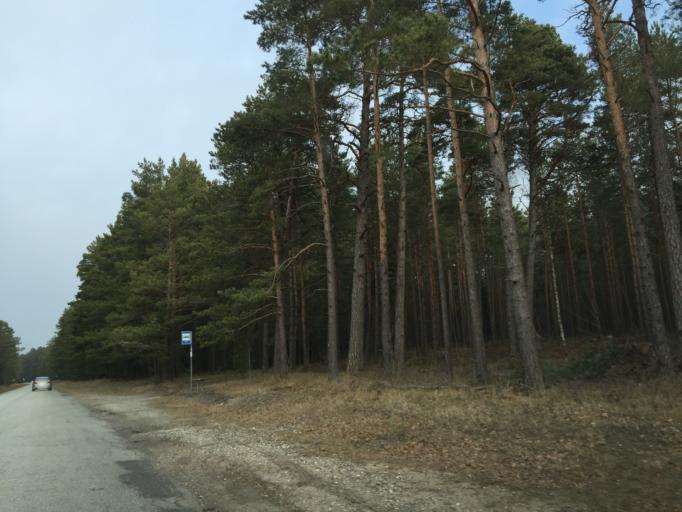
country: LV
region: Salacgrivas
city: Ainazi
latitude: 57.9358
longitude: 24.3917
